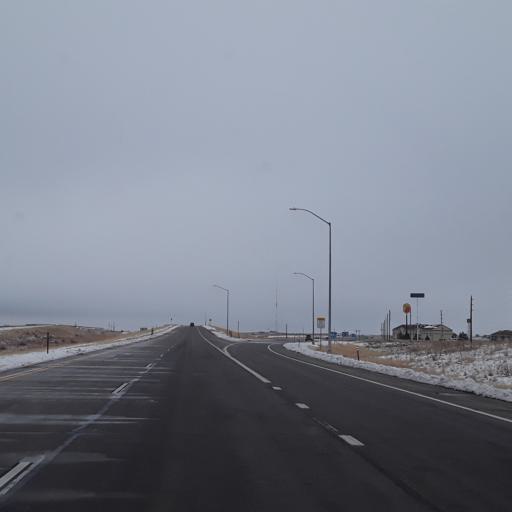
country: US
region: Colorado
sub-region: Logan County
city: Sterling
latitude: 40.6167
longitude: -103.1746
